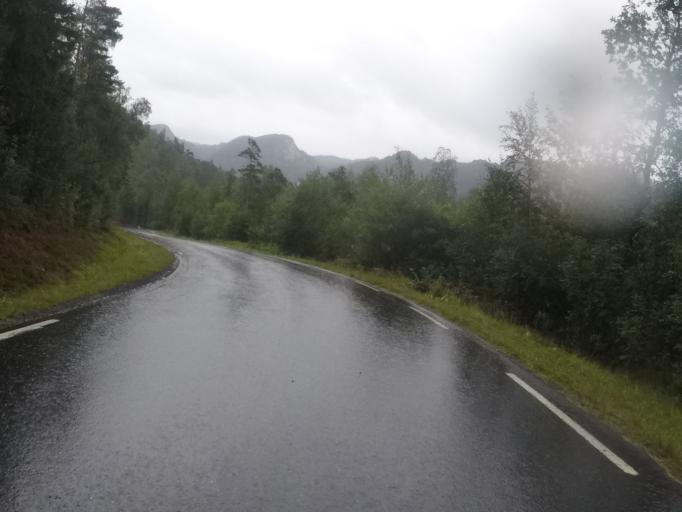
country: NO
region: Vest-Agder
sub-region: Lyngdal
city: Lyngdal
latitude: 58.2373
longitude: 7.1495
